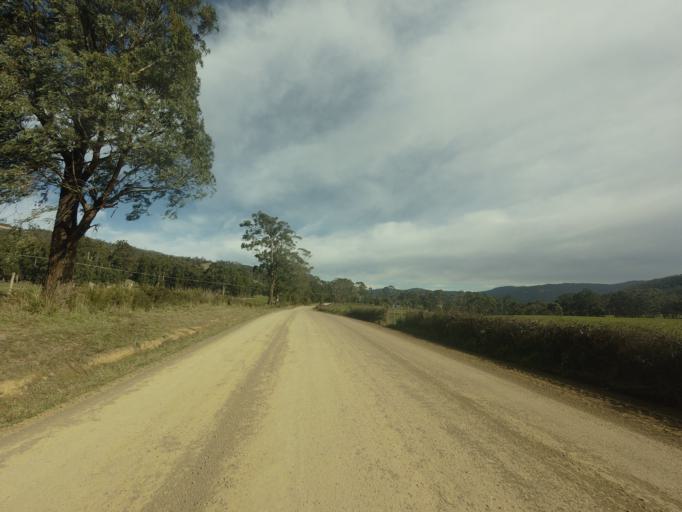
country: AU
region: Tasmania
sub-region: Huon Valley
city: Huonville
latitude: -43.0757
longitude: 147.0647
